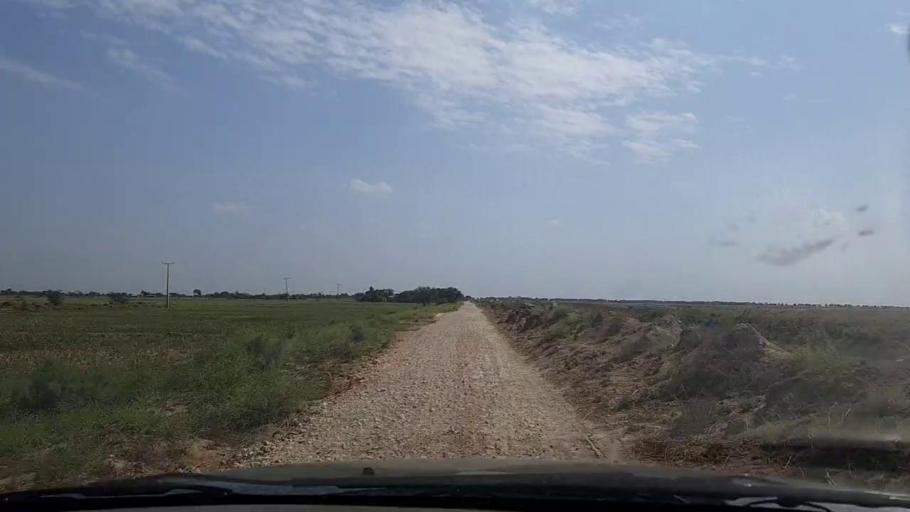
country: PK
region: Sindh
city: Mirpur Batoro
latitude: 24.5778
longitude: 68.1960
